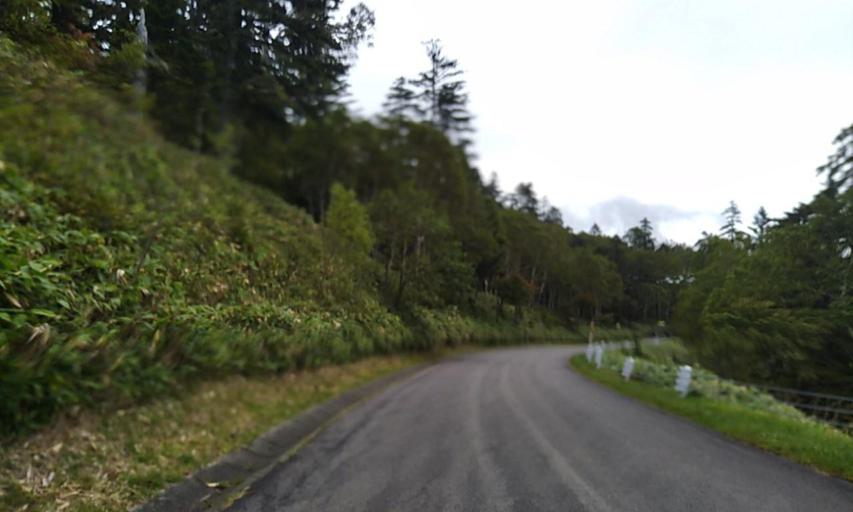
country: JP
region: Hokkaido
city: Bihoro
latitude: 43.5663
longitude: 144.2236
